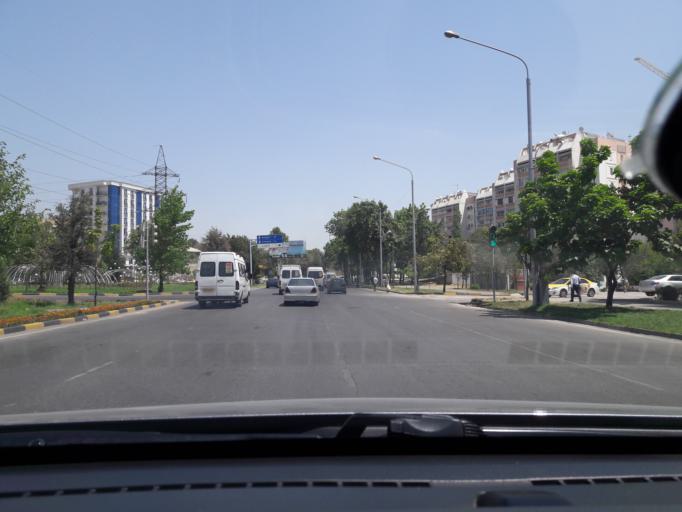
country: TJ
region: Dushanbe
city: Dushanbe
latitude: 38.5907
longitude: 68.7425
